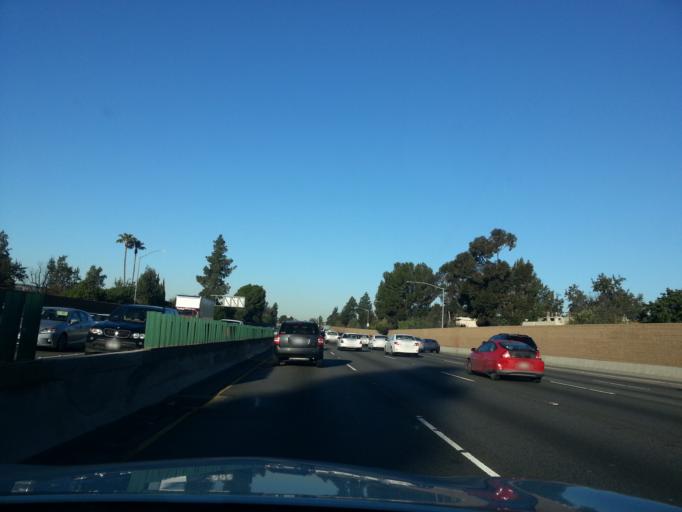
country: US
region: California
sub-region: Los Angeles County
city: Sherman Oaks
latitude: 34.1568
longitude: -118.4156
